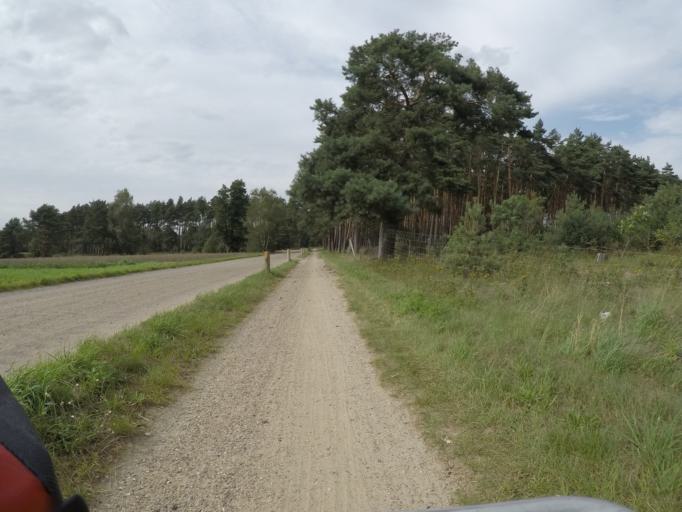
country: DE
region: Lower Saxony
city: Bardowick
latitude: 53.3143
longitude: 10.4008
